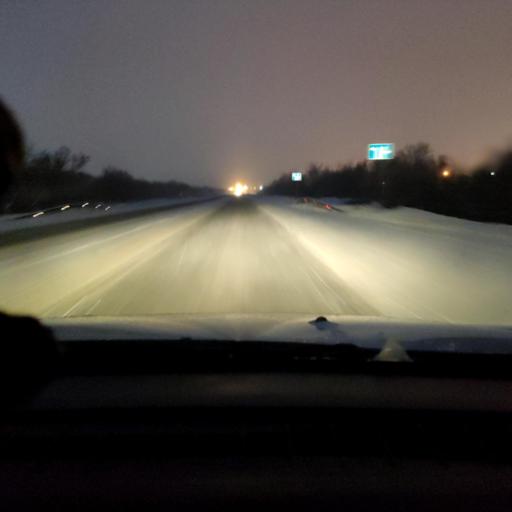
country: RU
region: Samara
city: Otradnyy
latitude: 53.3833
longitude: 51.3883
